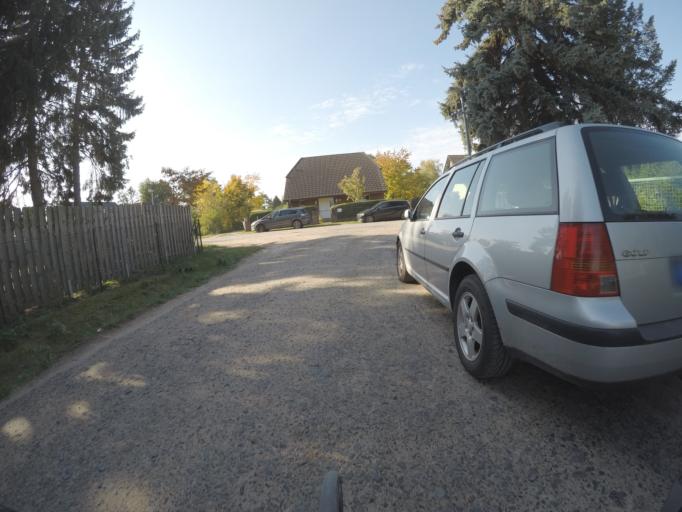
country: DE
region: Brandenburg
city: Oranienburg
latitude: 52.7233
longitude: 13.2385
